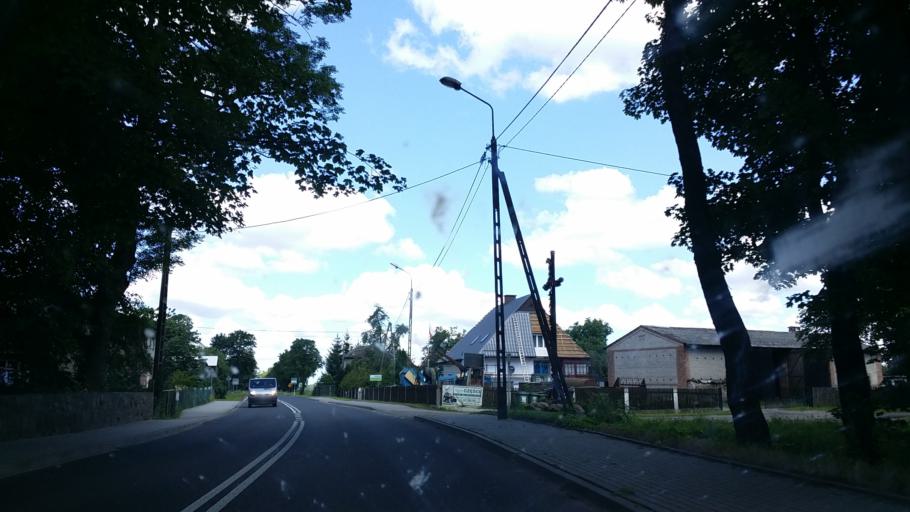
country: PL
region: West Pomeranian Voivodeship
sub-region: Powiat swidwinski
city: Swidwin
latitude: 53.8134
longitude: 15.7612
